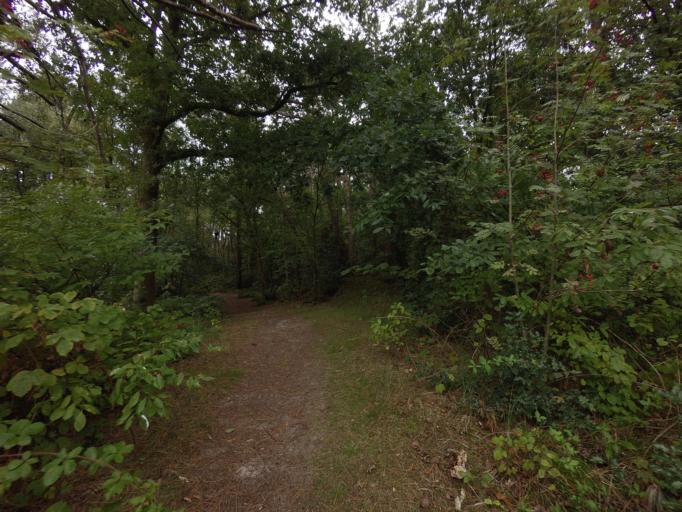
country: NL
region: Friesland
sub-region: Gemeente Schiermonnikoog
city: Schiermonnikoog
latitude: 53.4860
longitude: 6.1639
